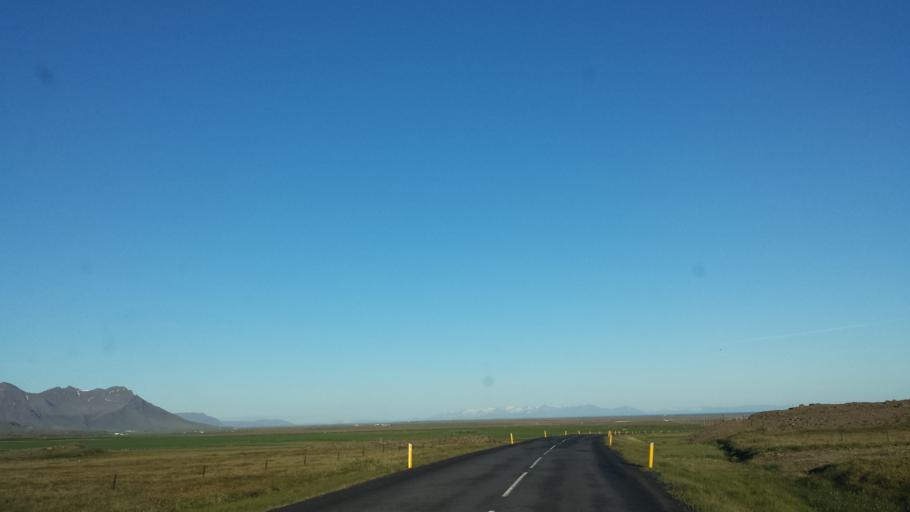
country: IS
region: West
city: Stykkisholmur
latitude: 64.8723
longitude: -22.7675
